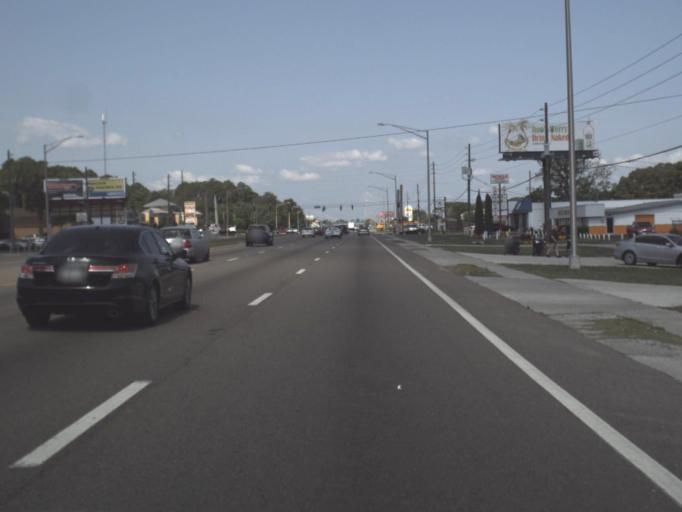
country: US
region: Florida
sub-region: Duval County
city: Jacksonville
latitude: 30.2868
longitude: -81.5461
